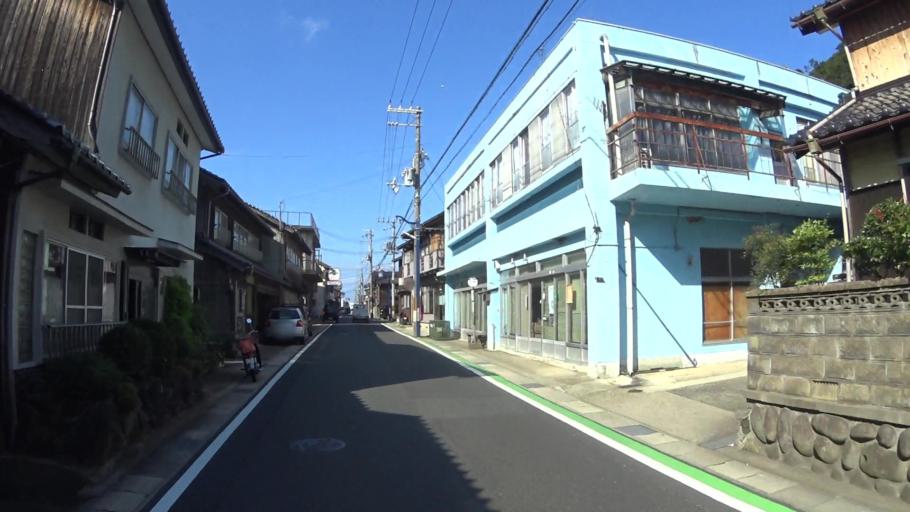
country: JP
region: Kyoto
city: Miyazu
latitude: 35.7367
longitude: 135.0946
